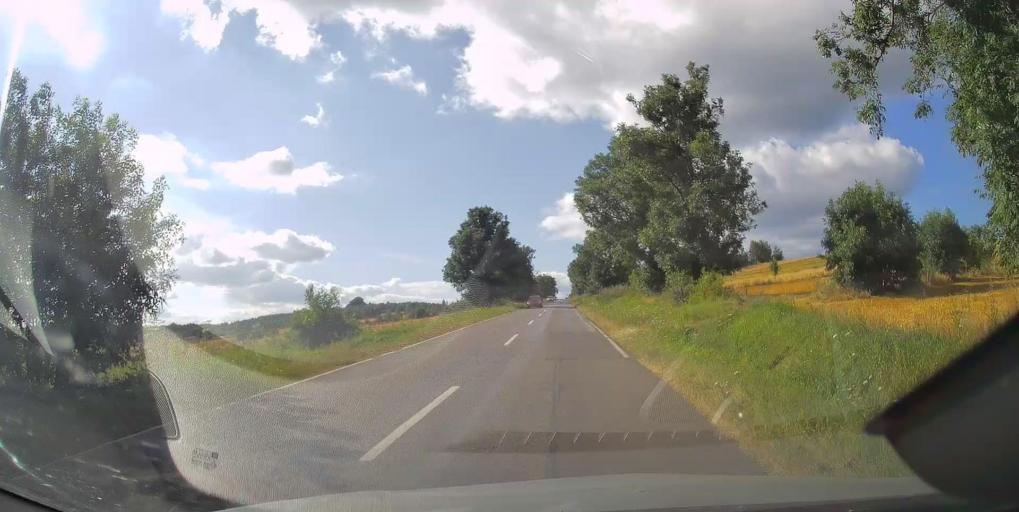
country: PL
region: Swietokrzyskie
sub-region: Powiat skarzyski
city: Suchedniow
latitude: 50.9851
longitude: 20.8702
